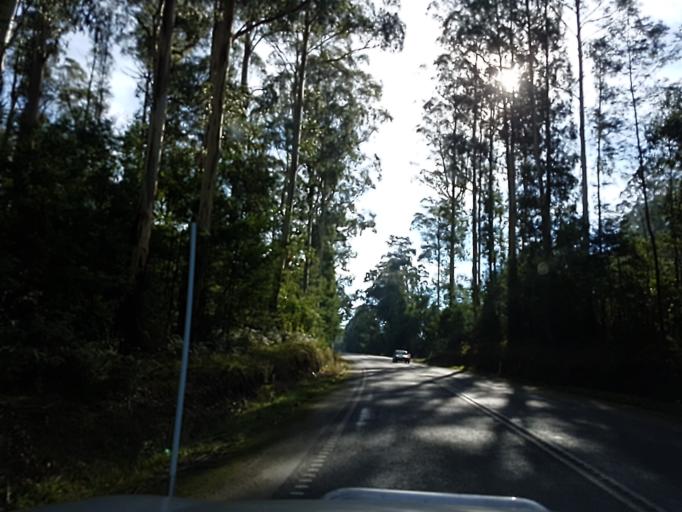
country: AU
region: Victoria
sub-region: Yarra Ranges
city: Yarra Glen
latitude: -37.5124
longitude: 145.4250
